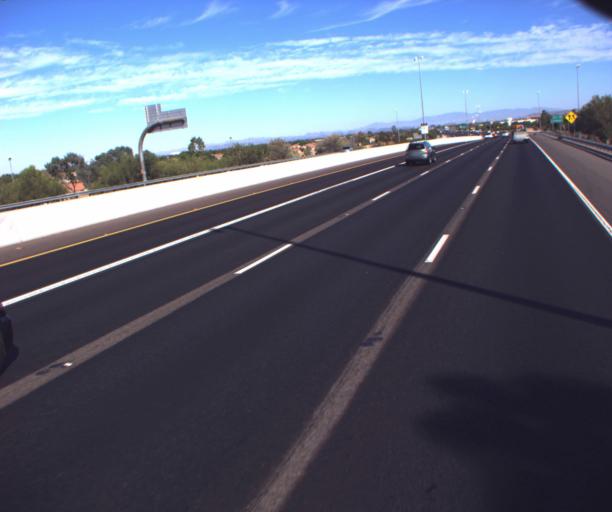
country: US
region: Arizona
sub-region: Maricopa County
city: Peoria
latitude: 33.5665
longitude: -112.2570
